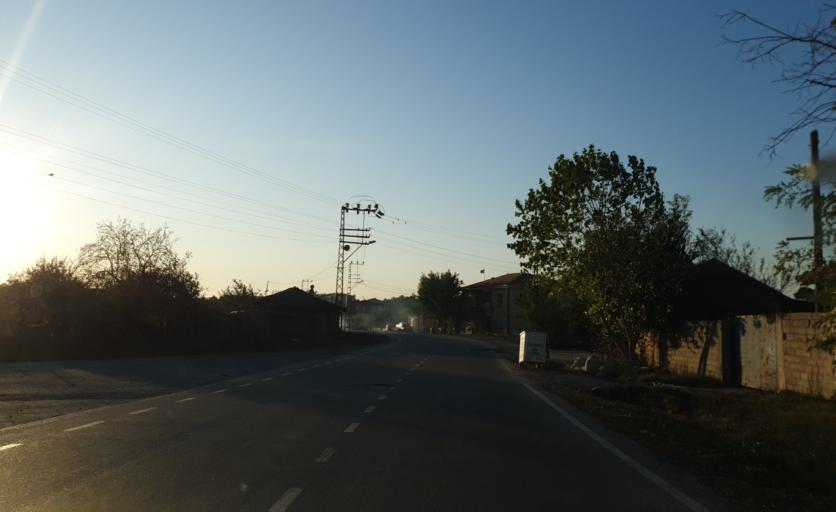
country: TR
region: Tekirdag
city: Beyazkoy
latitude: 41.3349
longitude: 27.7420
